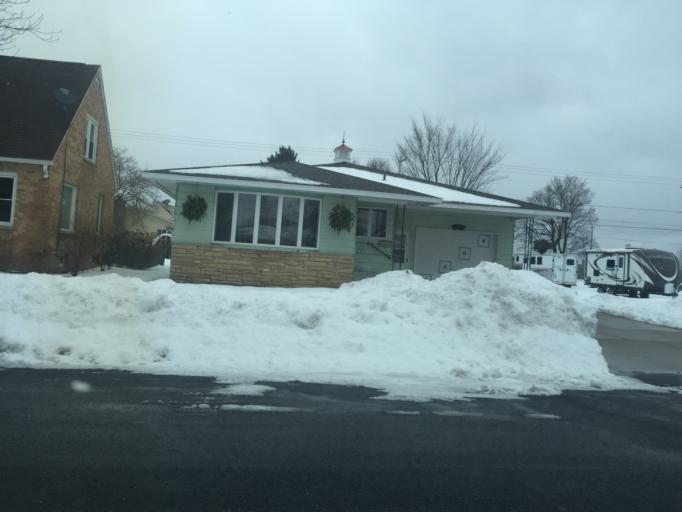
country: US
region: Wisconsin
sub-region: Marinette County
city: Marinette
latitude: 45.1144
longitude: -87.6309
